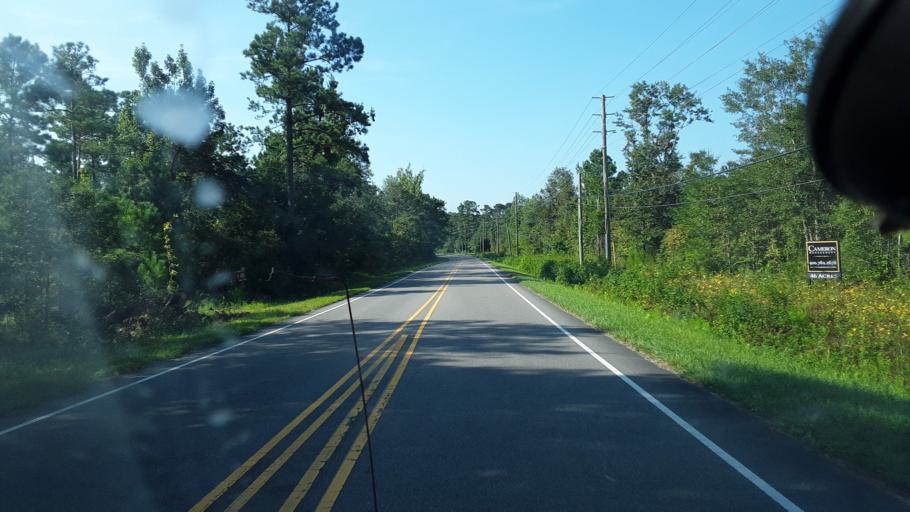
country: US
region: North Carolina
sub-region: Brunswick County
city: Belville
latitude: 34.1818
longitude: -77.9898
